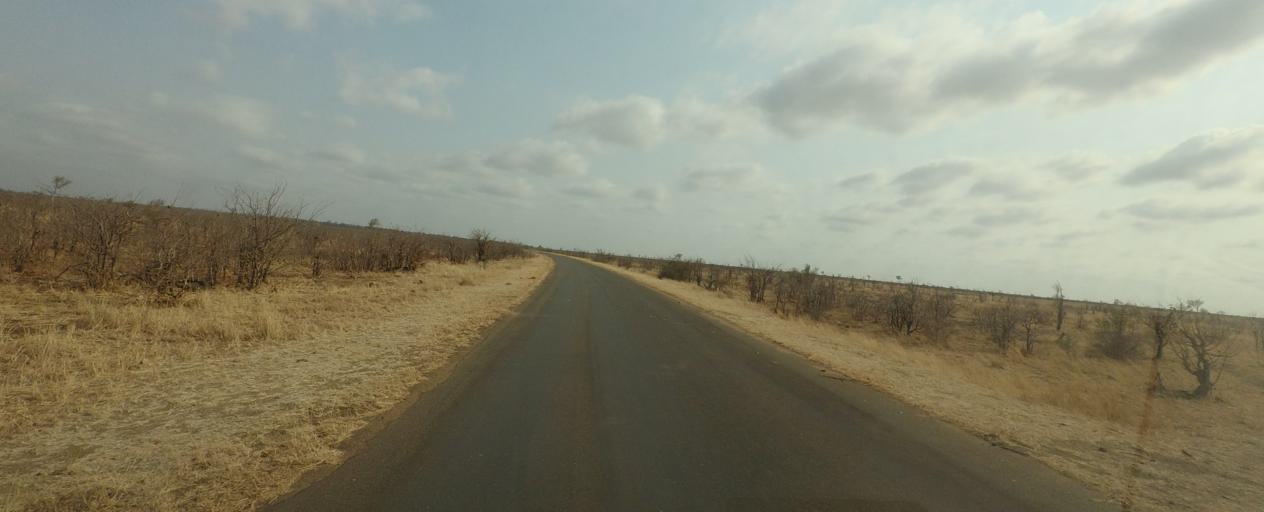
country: ZA
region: Limpopo
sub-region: Vhembe District Municipality
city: Mutale
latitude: -22.9018
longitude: 31.2530
